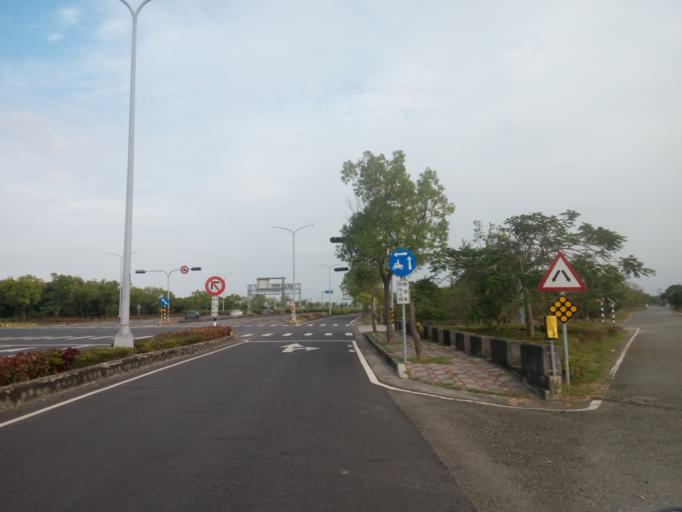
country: TW
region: Taiwan
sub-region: Chiayi
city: Taibao
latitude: 23.4827
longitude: 120.3514
